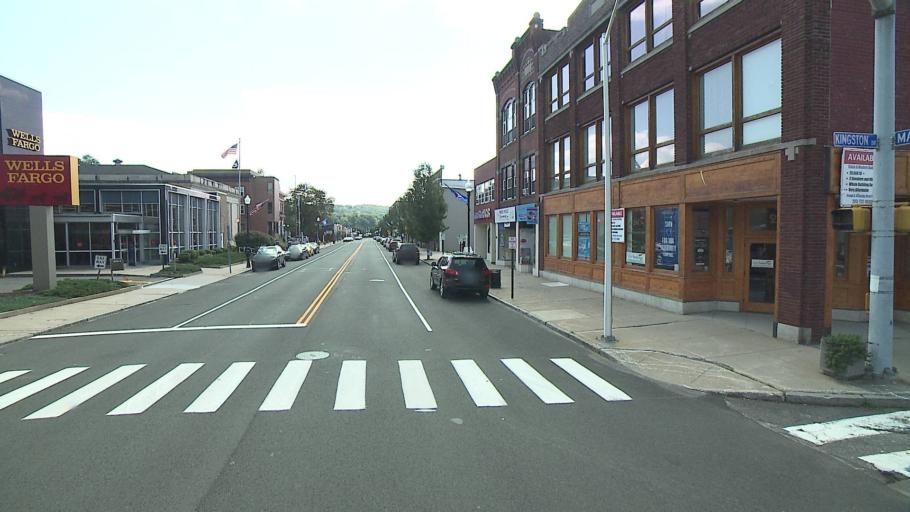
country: US
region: Connecticut
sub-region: New Haven County
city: Ansonia
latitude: 41.3437
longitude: -73.0790
